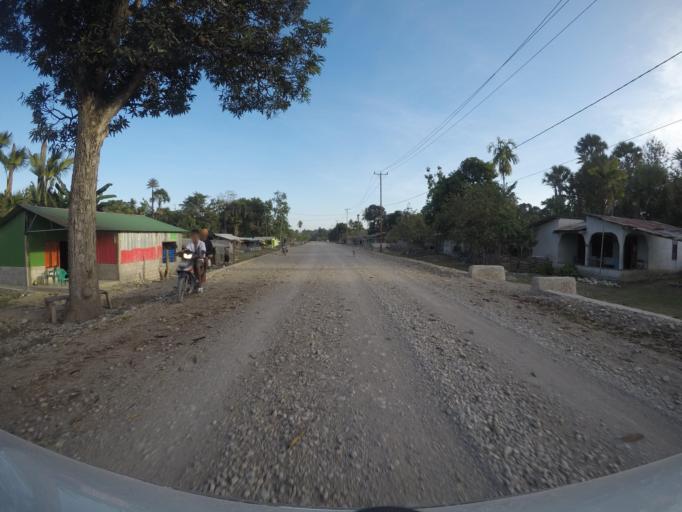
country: TL
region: Viqueque
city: Viqueque
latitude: -8.8663
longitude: 126.5074
